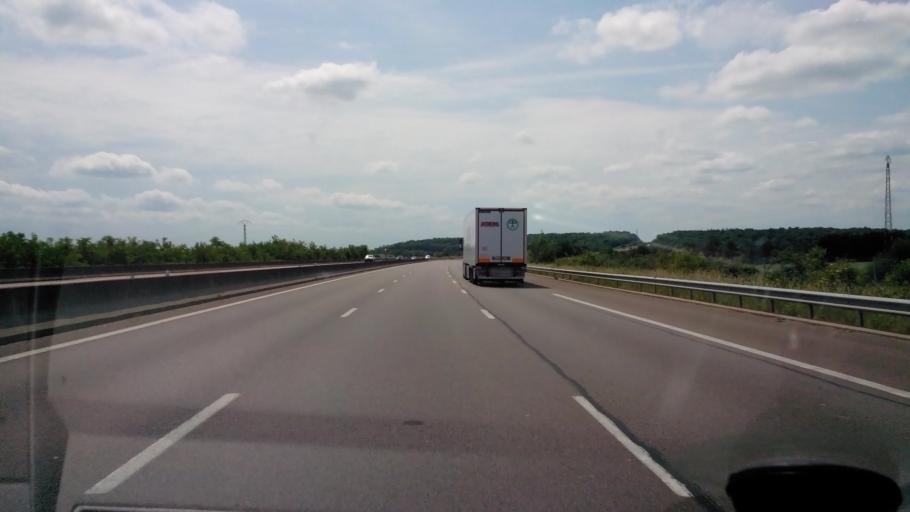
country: FR
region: Bourgogne
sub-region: Departement de la Cote-d'Or
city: Selongey
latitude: 47.5798
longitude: 5.2103
